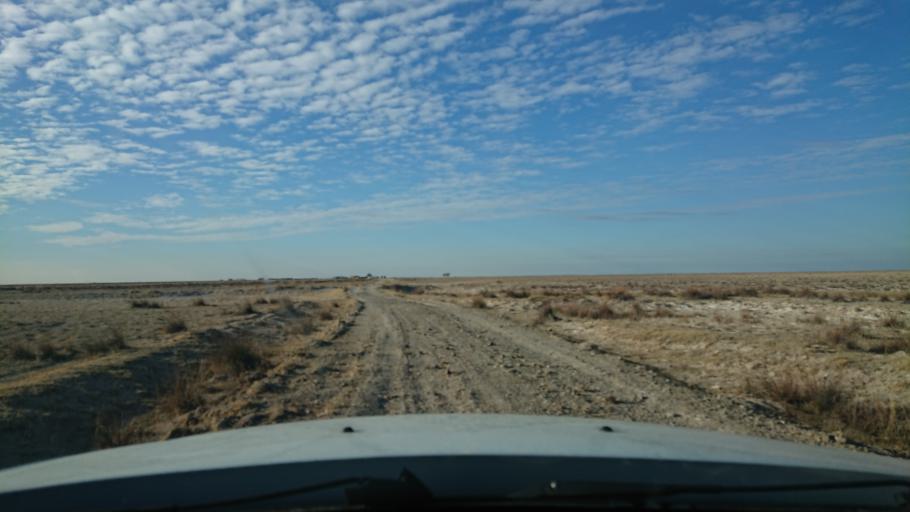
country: TR
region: Aksaray
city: Eskil
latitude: 38.5626
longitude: 33.3063
